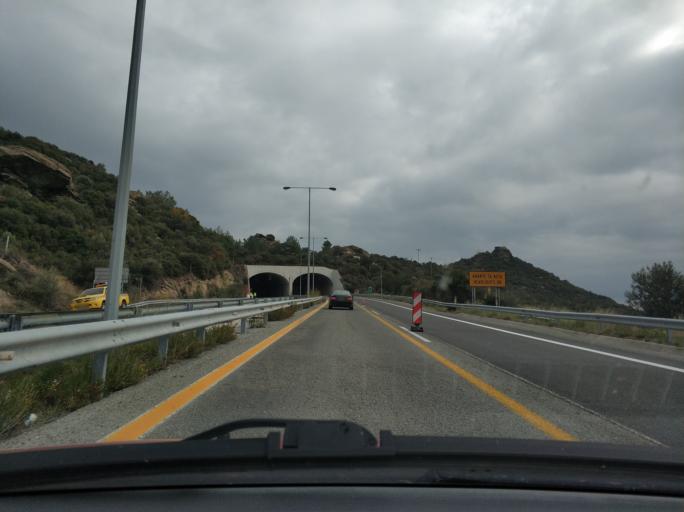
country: GR
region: East Macedonia and Thrace
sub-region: Nomos Kavalas
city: Palaio Tsifliki
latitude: 40.9100
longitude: 24.3539
